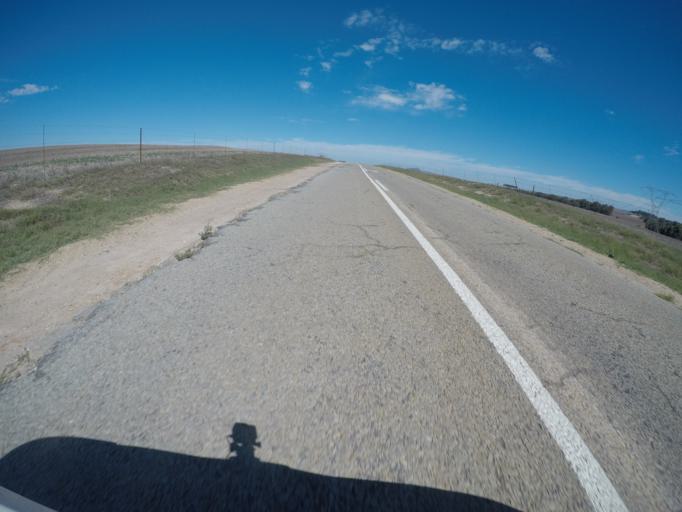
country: ZA
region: Western Cape
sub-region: City of Cape Town
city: Atlantis
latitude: -33.6004
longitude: 18.6416
